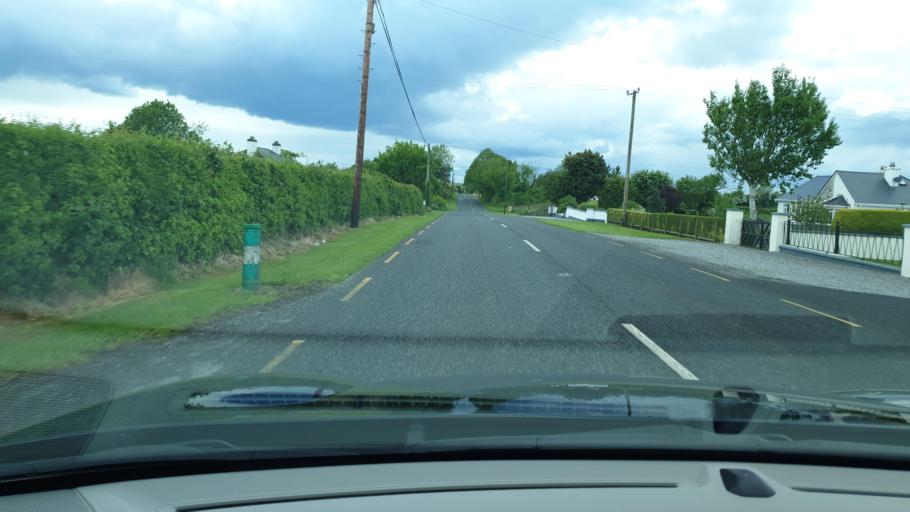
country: IE
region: Leinster
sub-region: Uibh Fhaili
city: Clara
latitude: 53.2338
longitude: -7.6328
